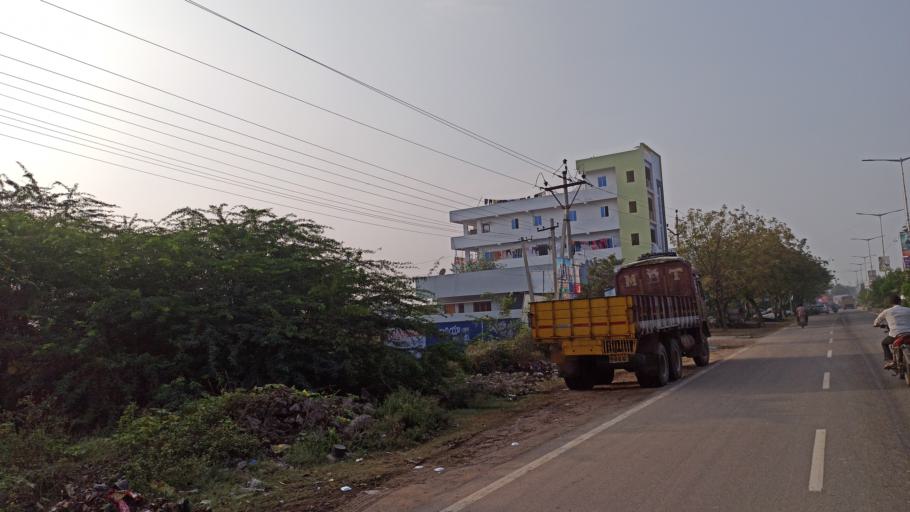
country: IN
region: Andhra Pradesh
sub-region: Guntur
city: Narasaraopet
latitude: 16.2495
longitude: 80.0571
